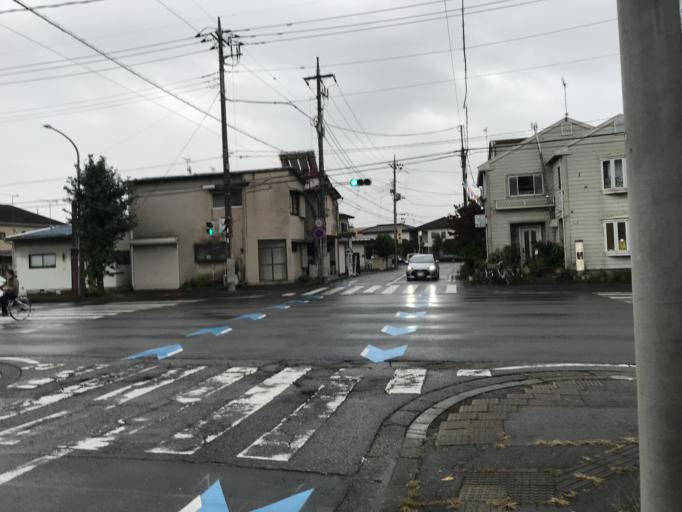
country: JP
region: Tochigi
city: Utsunomiya-shi
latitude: 36.5517
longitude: 139.8847
